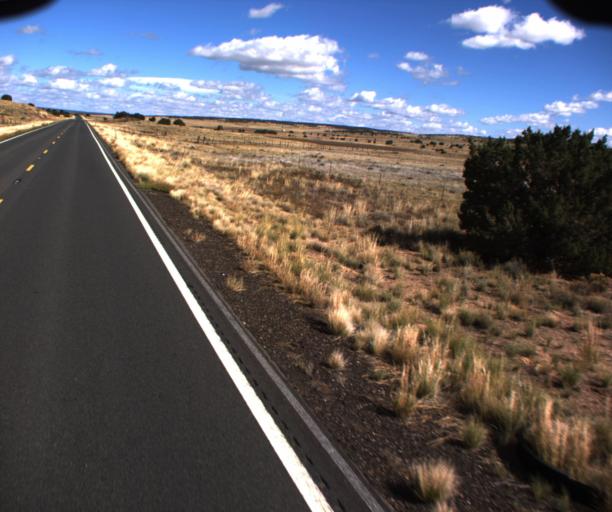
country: US
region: Arizona
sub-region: Apache County
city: Houck
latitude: 34.9511
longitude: -109.2313
